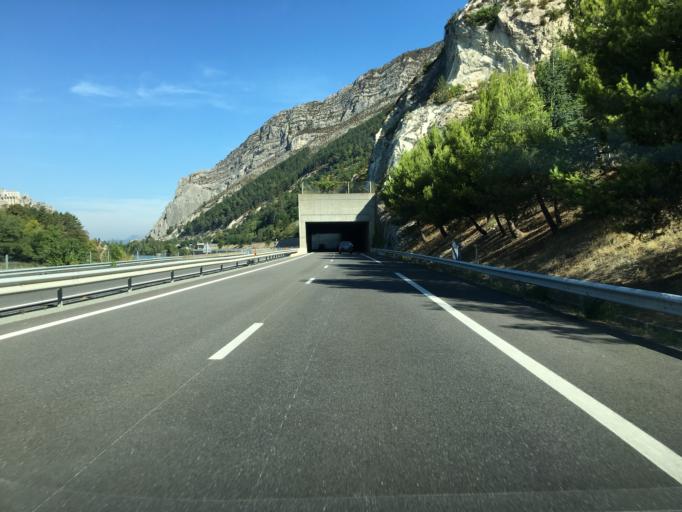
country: FR
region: Provence-Alpes-Cote d'Azur
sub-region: Departement des Alpes-de-Haute-Provence
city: Sisteron
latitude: 44.1904
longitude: 5.9548
